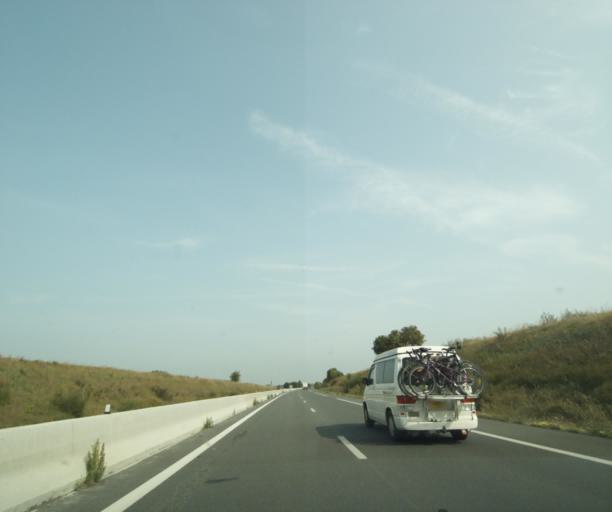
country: FR
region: Pays de la Loire
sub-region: Departement de la Sarthe
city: Beaumont-sur-Sarthe
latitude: 48.2505
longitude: 0.1622
